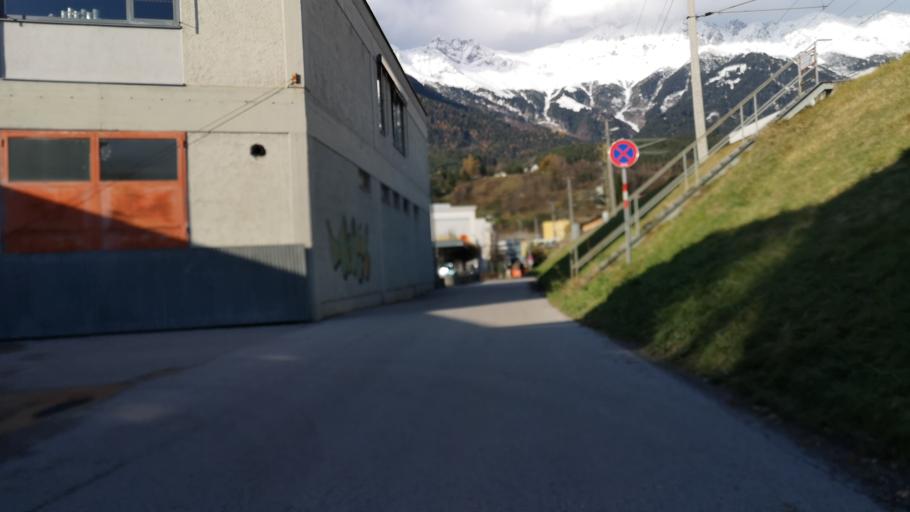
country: AT
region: Tyrol
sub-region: Innsbruck Stadt
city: Innsbruck
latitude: 47.2617
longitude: 11.3735
